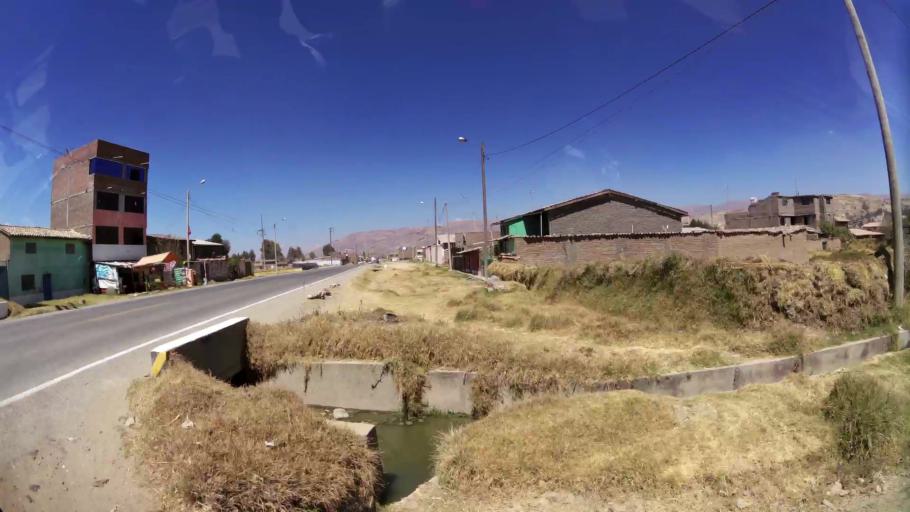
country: PE
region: Junin
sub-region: Provincia de Jauja
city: Jauja
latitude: -11.7671
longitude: -75.4938
